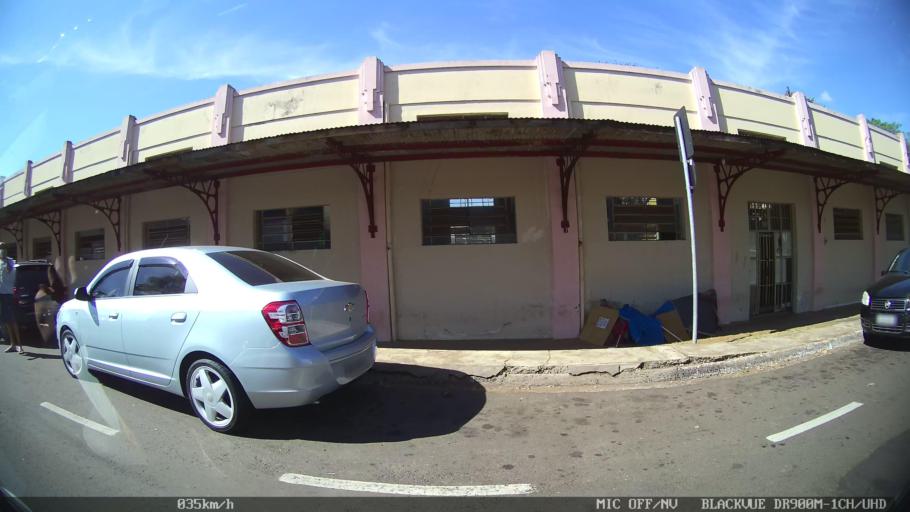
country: BR
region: Sao Paulo
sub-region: Franca
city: Franca
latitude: -20.5335
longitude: -47.4129
